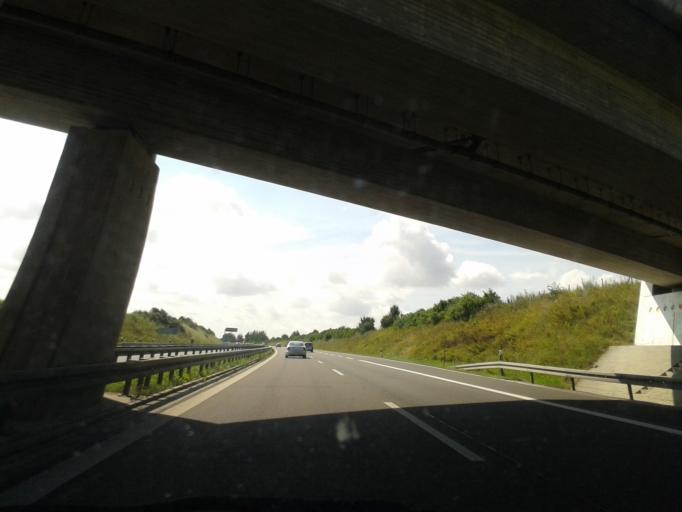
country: DE
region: Brandenburg
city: Schenkenberg
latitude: 53.3566
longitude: 13.9741
